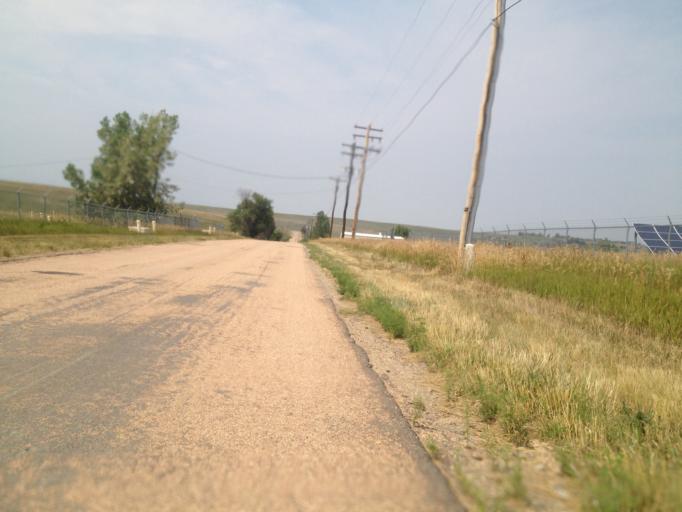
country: US
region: Colorado
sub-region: Boulder County
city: Superior
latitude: 39.9511
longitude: -105.1989
